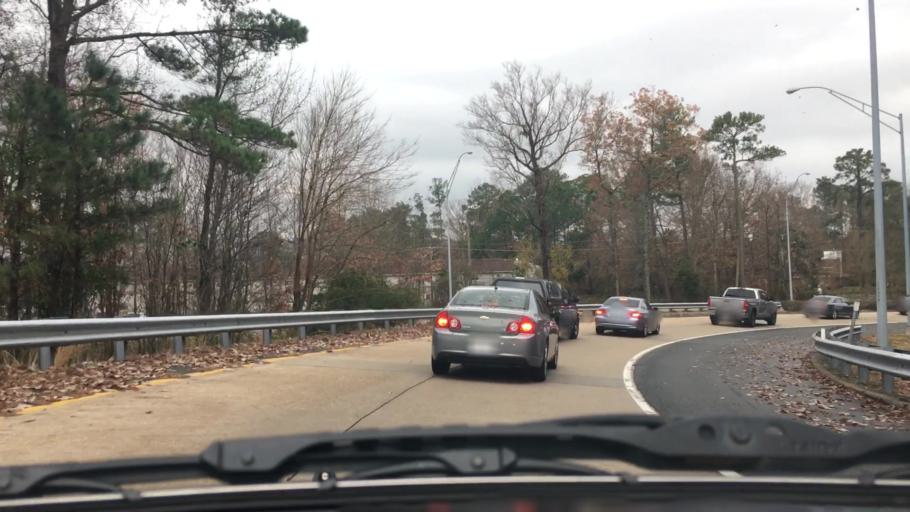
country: US
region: Virginia
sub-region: City of Chesapeake
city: Chesapeake
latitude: 36.8331
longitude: -76.1359
